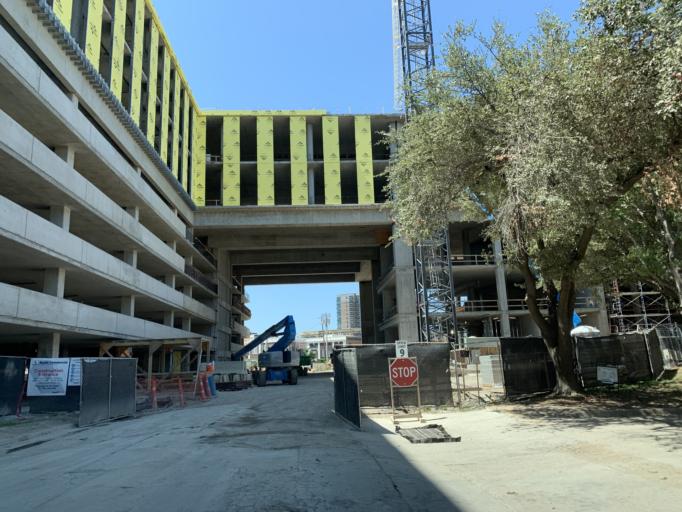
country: US
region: Texas
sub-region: Dallas County
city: Dallas
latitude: 32.7876
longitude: -96.7749
